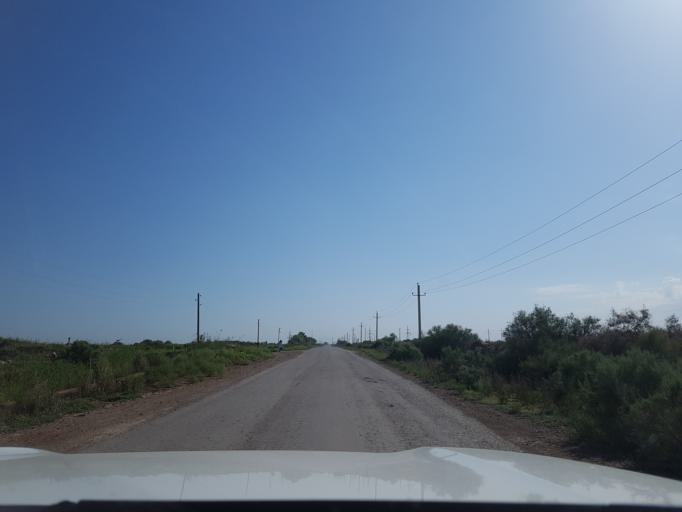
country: TM
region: Dasoguz
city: Koeneuergench
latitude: 42.0943
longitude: 58.8937
